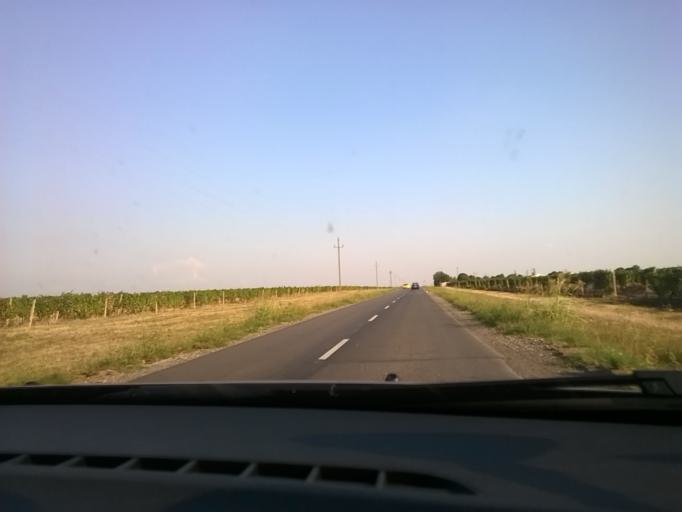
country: RS
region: Autonomna Pokrajina Vojvodina
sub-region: Juznobanatski Okrug
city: Vrsac
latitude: 45.1072
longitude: 21.3150
